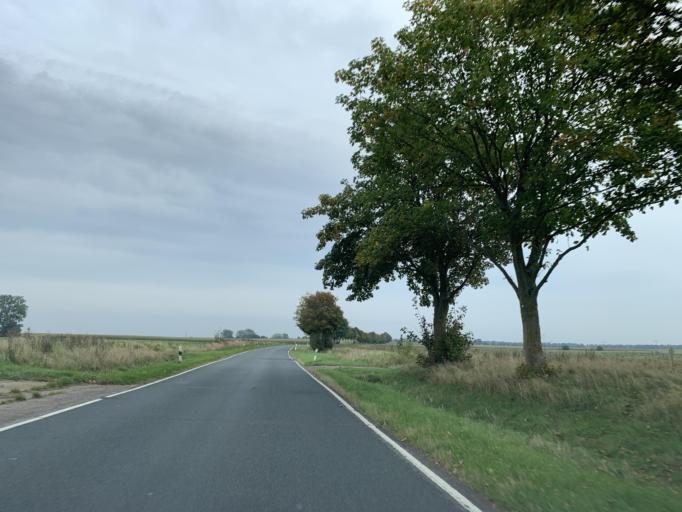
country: DE
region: Mecklenburg-Vorpommern
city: Woldegk
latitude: 53.3287
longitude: 13.5559
